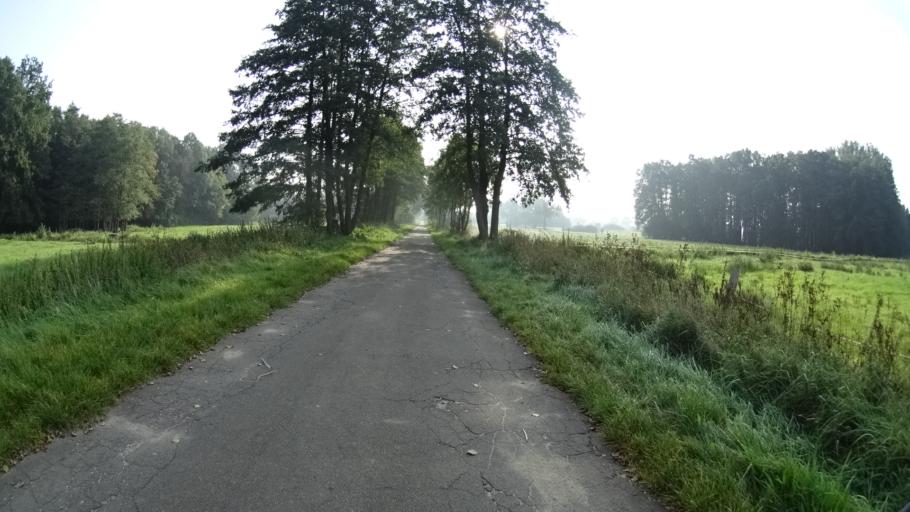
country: DE
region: Lower Saxony
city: Reppenstedt
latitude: 53.2298
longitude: 10.3679
